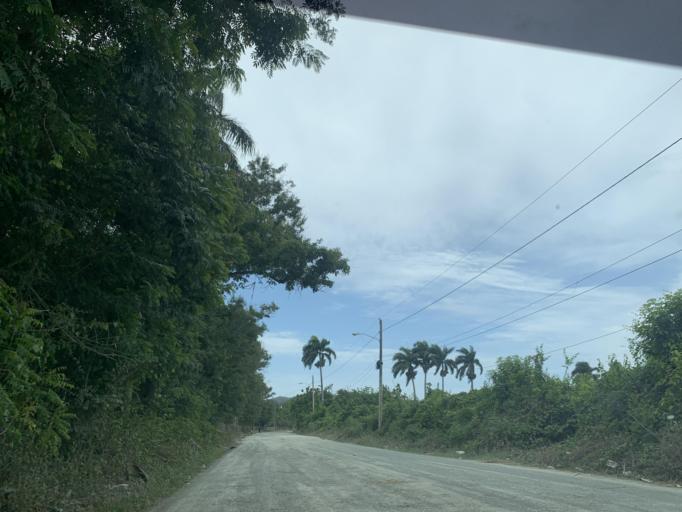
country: DO
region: Puerto Plata
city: Imbert
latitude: 19.8207
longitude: -70.7817
